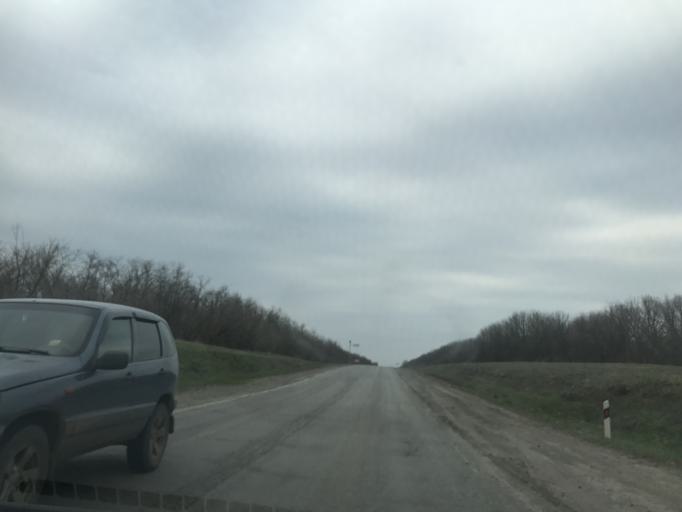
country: RU
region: Rostov
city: Krasyukovskaya
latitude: 47.5801
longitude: 40.1486
